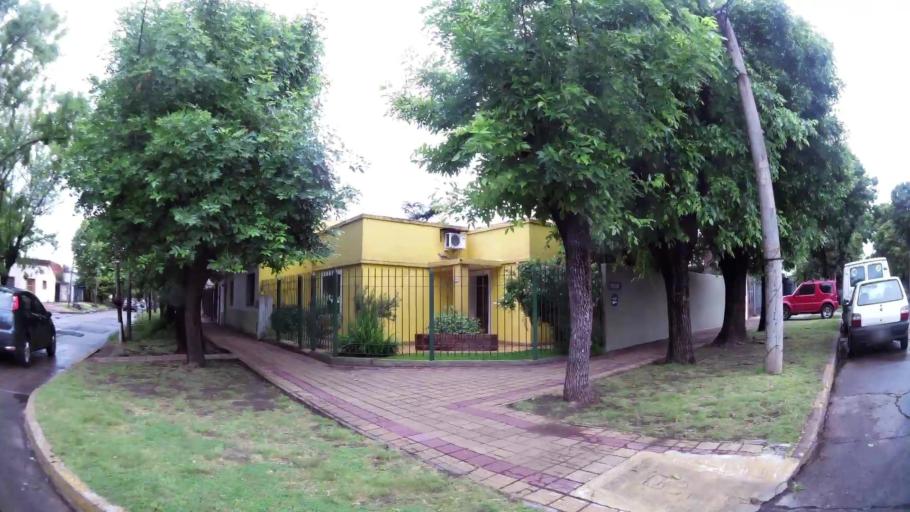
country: AR
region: Buenos Aires
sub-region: Partido de Lomas de Zamora
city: Lomas de Zamora
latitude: -34.7579
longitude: -58.3871
